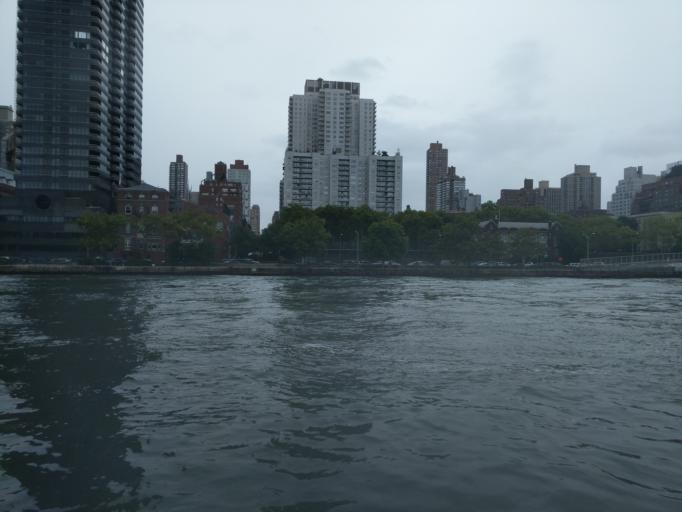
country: US
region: New York
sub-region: Queens County
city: Long Island City
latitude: 40.7679
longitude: -73.9480
